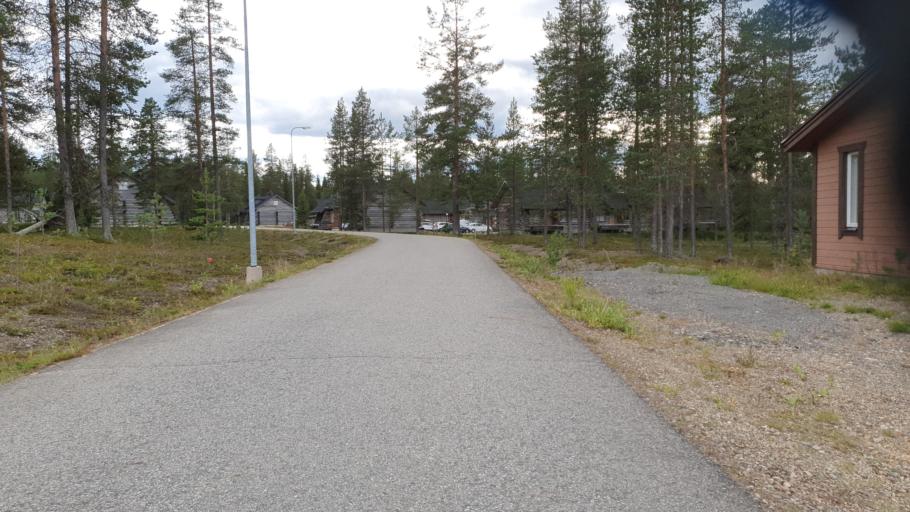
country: FI
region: Lapland
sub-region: Tunturi-Lappi
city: Kolari
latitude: 67.5962
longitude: 24.1503
